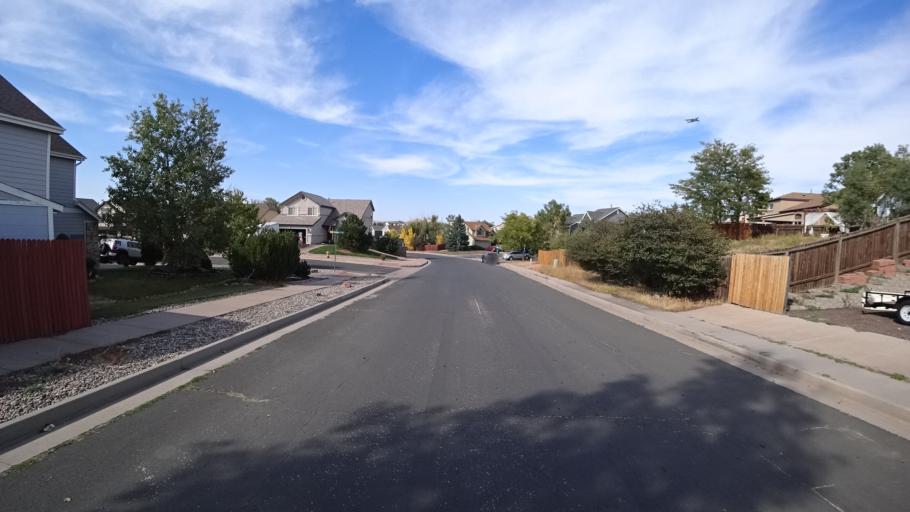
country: US
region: Colorado
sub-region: El Paso County
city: Cimarron Hills
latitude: 38.9037
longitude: -104.6944
